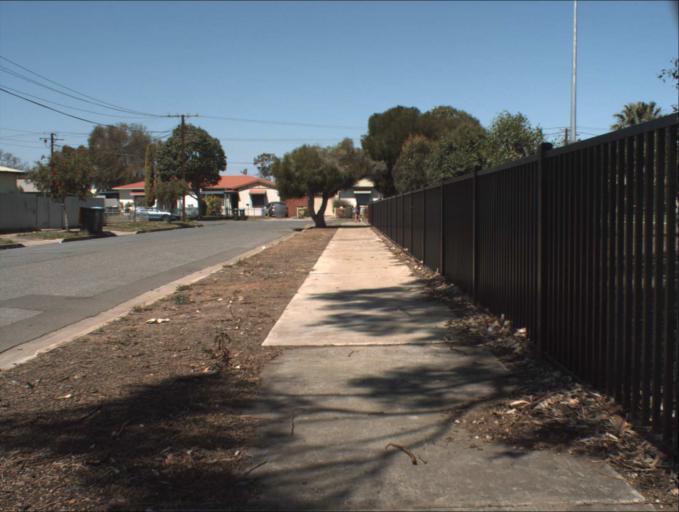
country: AU
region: South Australia
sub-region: Port Adelaide Enfield
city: Birkenhead
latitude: -34.8047
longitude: 138.5049
